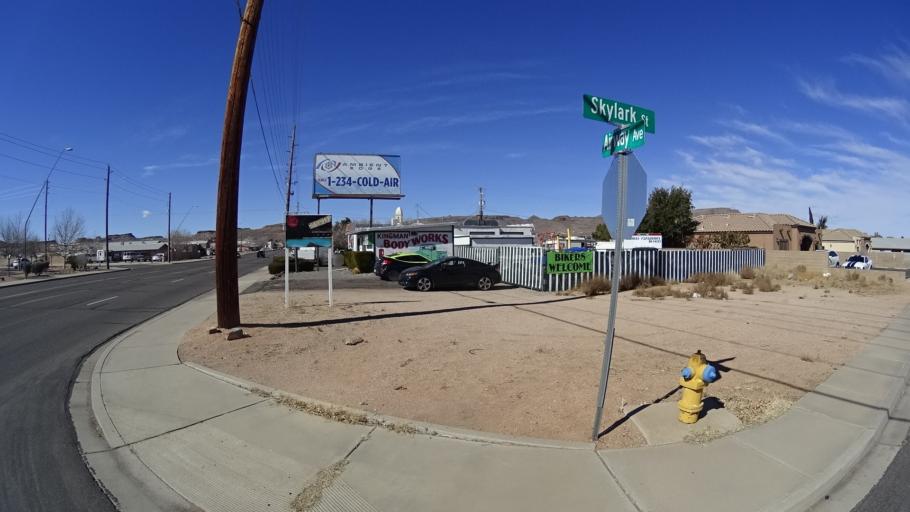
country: US
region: Arizona
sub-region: Mohave County
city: New Kingman-Butler
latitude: 35.2250
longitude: -114.0284
